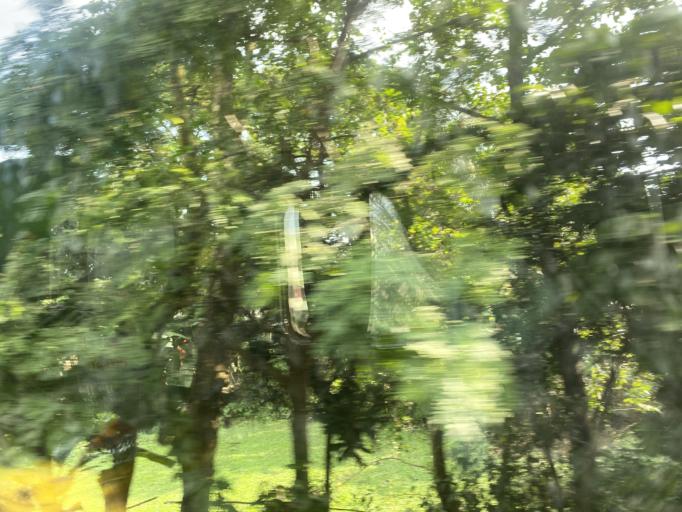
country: BD
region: Dhaka
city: Bhairab Bazar
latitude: 23.9657
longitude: 91.1167
